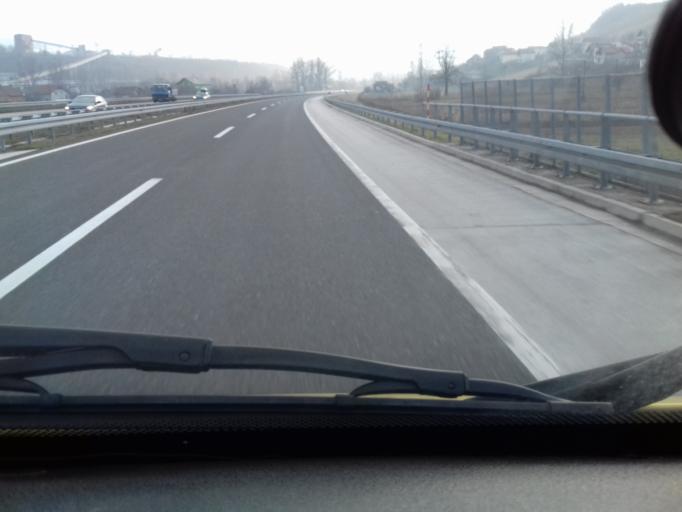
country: BA
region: Federation of Bosnia and Herzegovina
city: Kakanj
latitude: 44.1101
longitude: 18.1114
